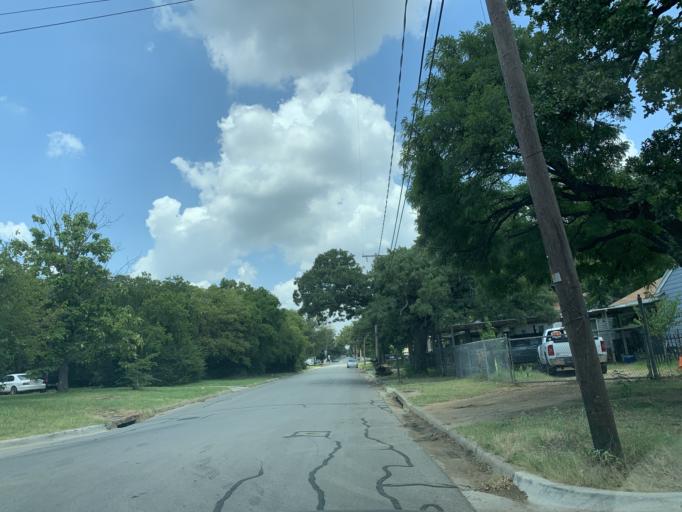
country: US
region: Texas
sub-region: Tarrant County
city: Forest Hill
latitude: 32.7328
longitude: -97.2566
